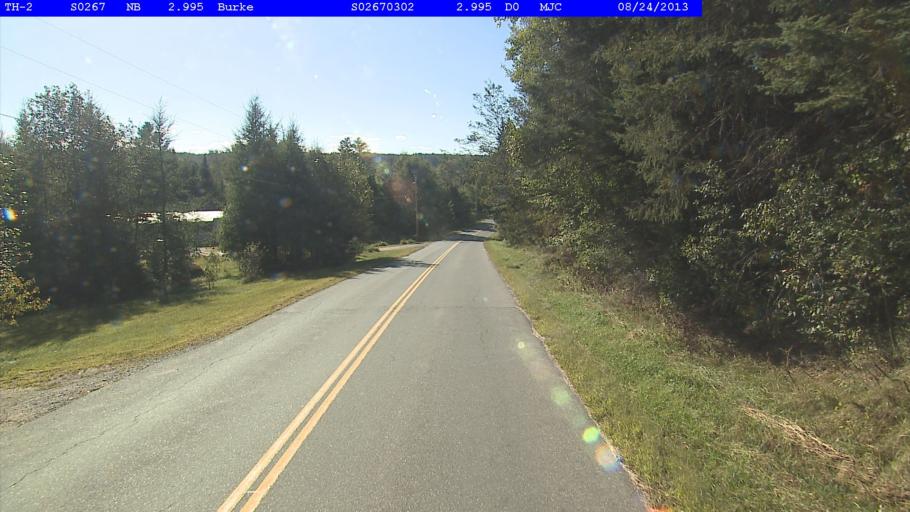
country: US
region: Vermont
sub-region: Caledonia County
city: Lyndonville
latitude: 44.6225
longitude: -71.9540
